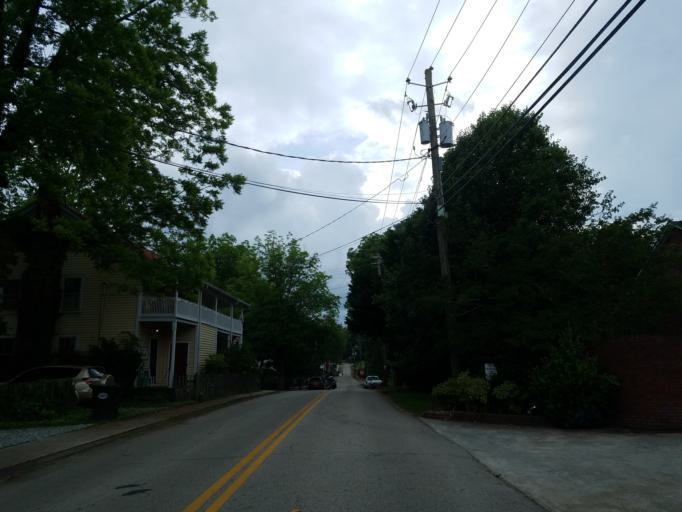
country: US
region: Georgia
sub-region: Lumpkin County
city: Dahlonega
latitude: 34.5347
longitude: -83.9847
